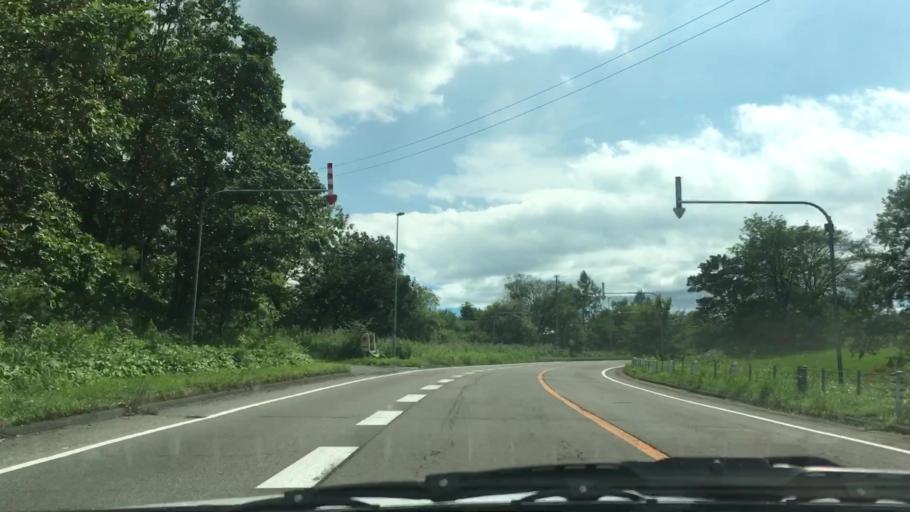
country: JP
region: Hokkaido
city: Otofuke
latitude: 43.2784
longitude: 143.4066
